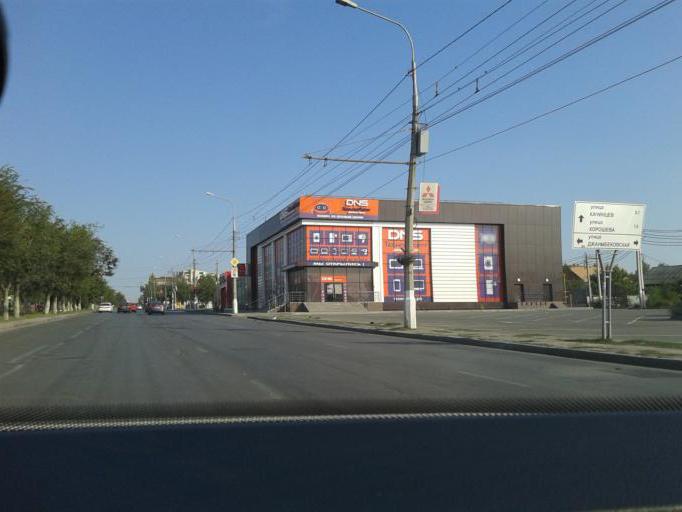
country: RU
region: Volgograd
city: Volgograd
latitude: 48.7287
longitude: 44.4989
